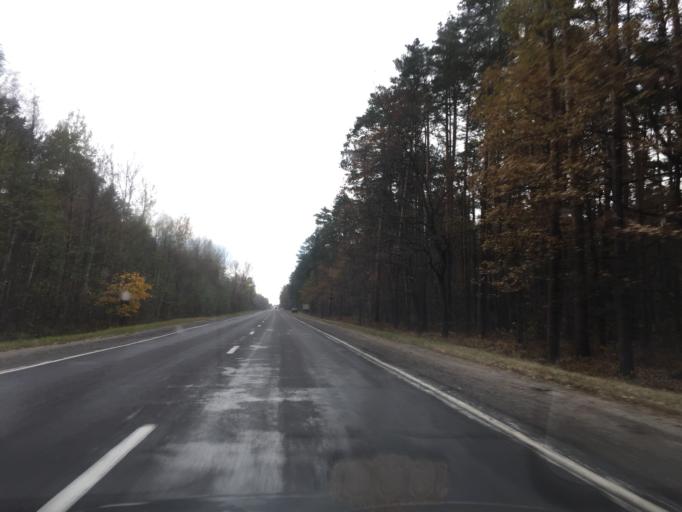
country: BY
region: Gomel
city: Gomel
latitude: 52.4025
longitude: 30.8291
